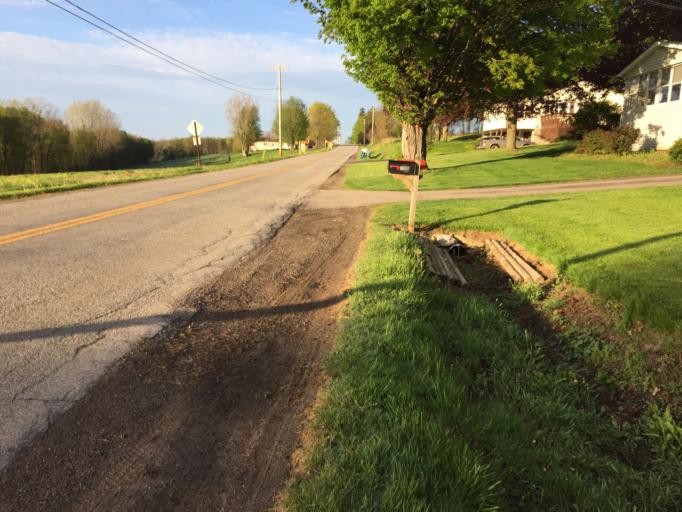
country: US
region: New York
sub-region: Wayne County
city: Marion
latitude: 43.1404
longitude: -77.1704
